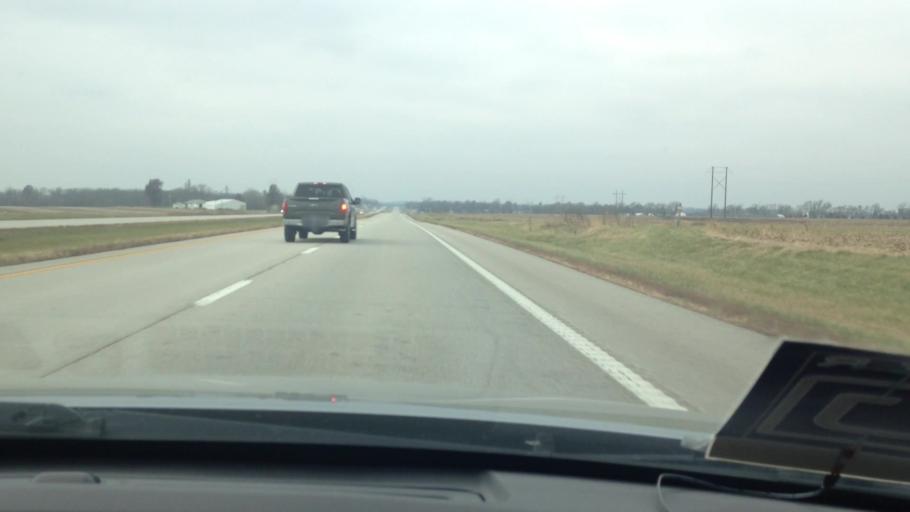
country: US
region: Missouri
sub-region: Cass County
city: Garden City
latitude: 38.5877
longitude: -94.2323
